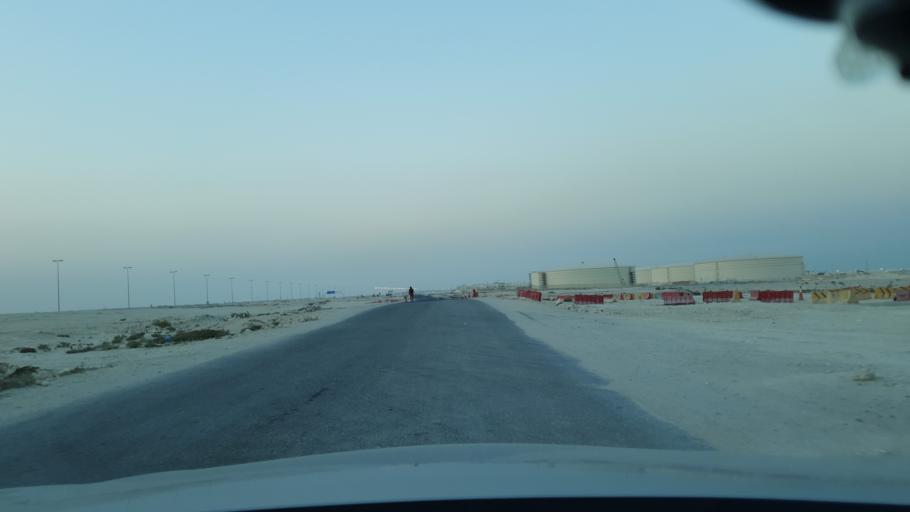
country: BH
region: Central Governorate
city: Dar Kulayb
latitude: 25.9724
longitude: 50.6021
